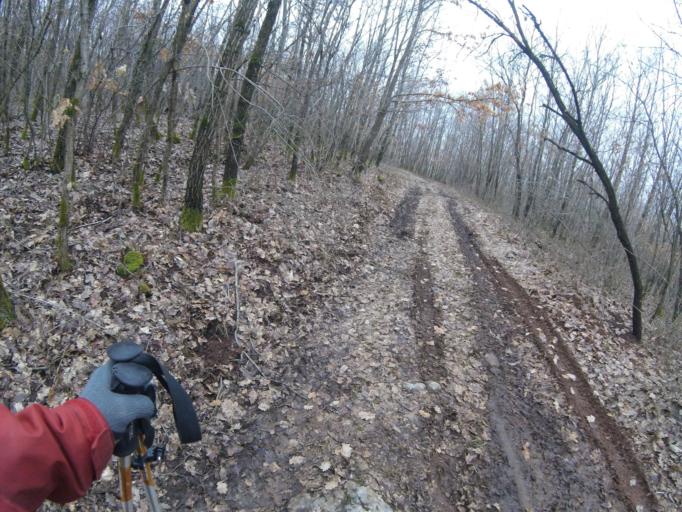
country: HU
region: Borsod-Abauj-Zemplen
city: Rudabanya
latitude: 48.4607
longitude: 20.6122
